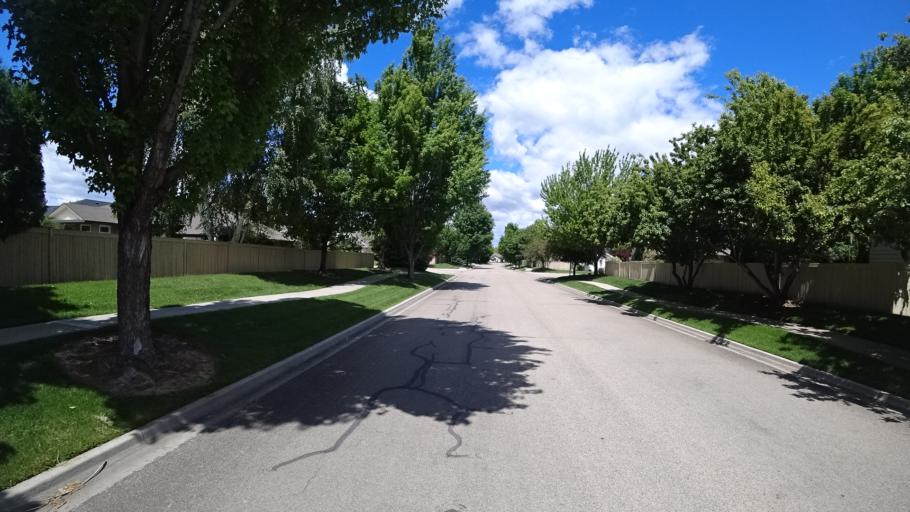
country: US
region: Idaho
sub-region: Ada County
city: Eagle
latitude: 43.6572
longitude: -116.3615
